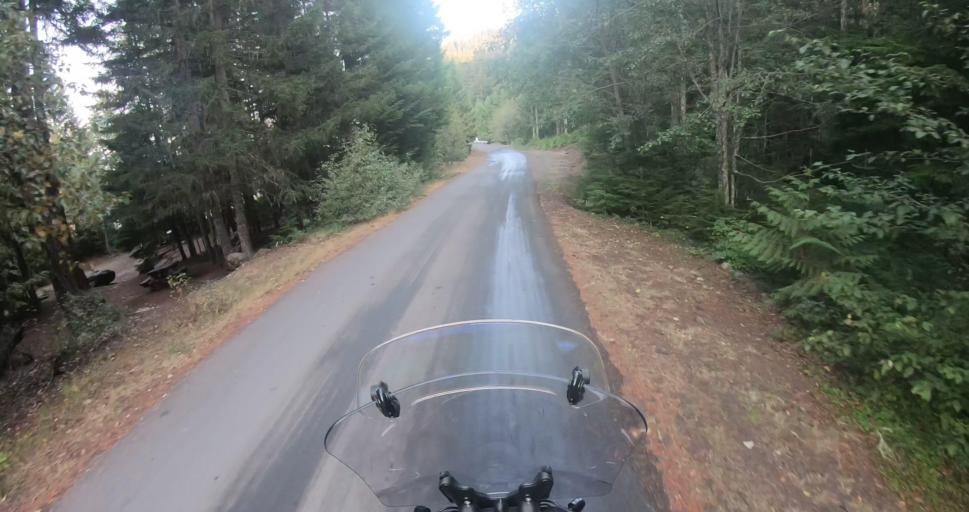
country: US
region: Oregon
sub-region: Hood River County
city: Odell
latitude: 45.4572
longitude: -121.6628
